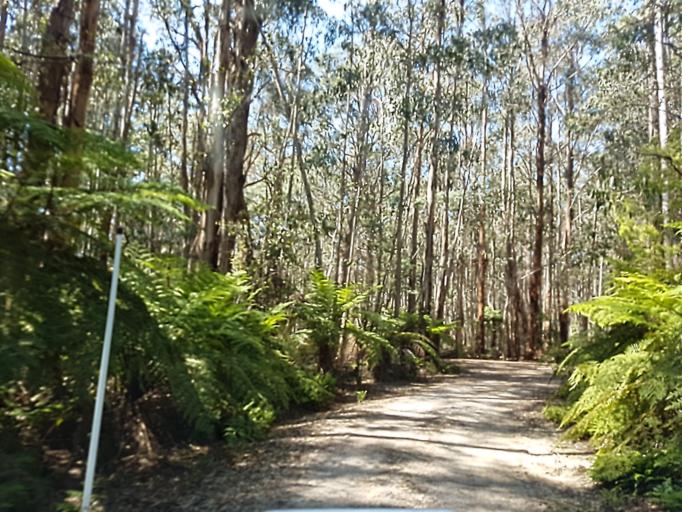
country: AU
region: Victoria
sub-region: East Gippsland
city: Lakes Entrance
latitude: -37.2916
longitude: 148.3246
